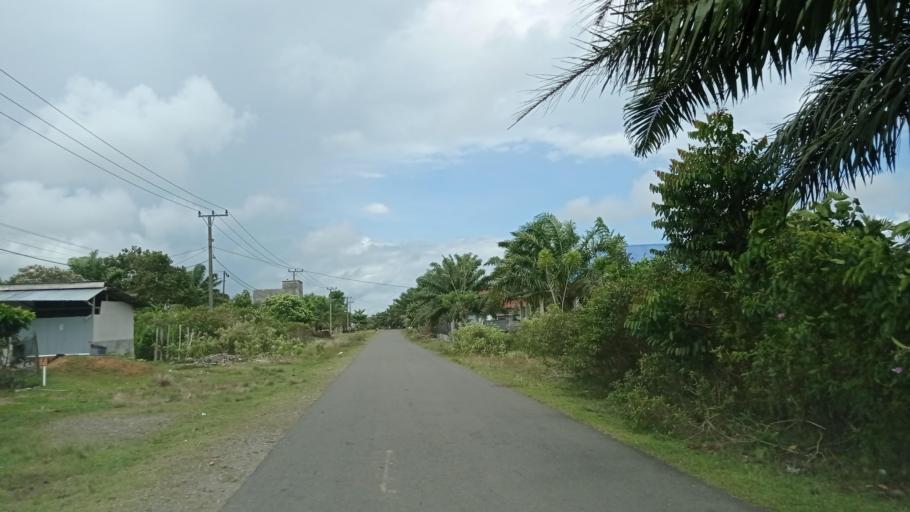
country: ID
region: Bengkulu
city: Ipuh
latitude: -2.5668
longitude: 101.1150
